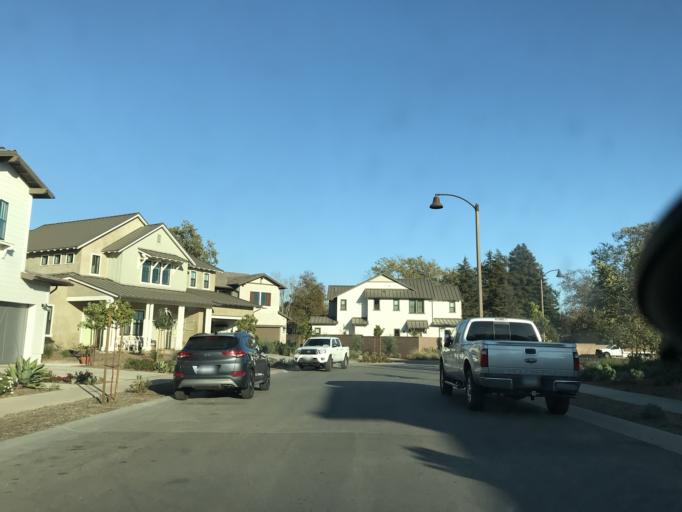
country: US
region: California
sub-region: Santa Barbara County
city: Goleta
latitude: 34.4511
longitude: -119.8134
